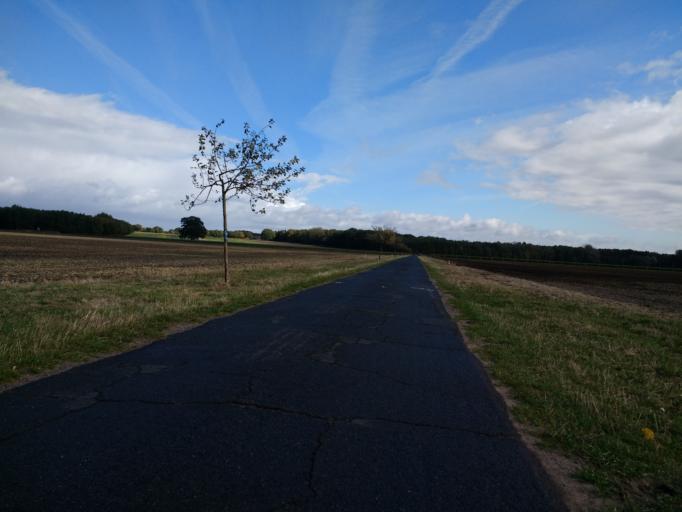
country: DE
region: Lower Saxony
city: Wagenhoff
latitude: 52.4950
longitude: 10.4953
